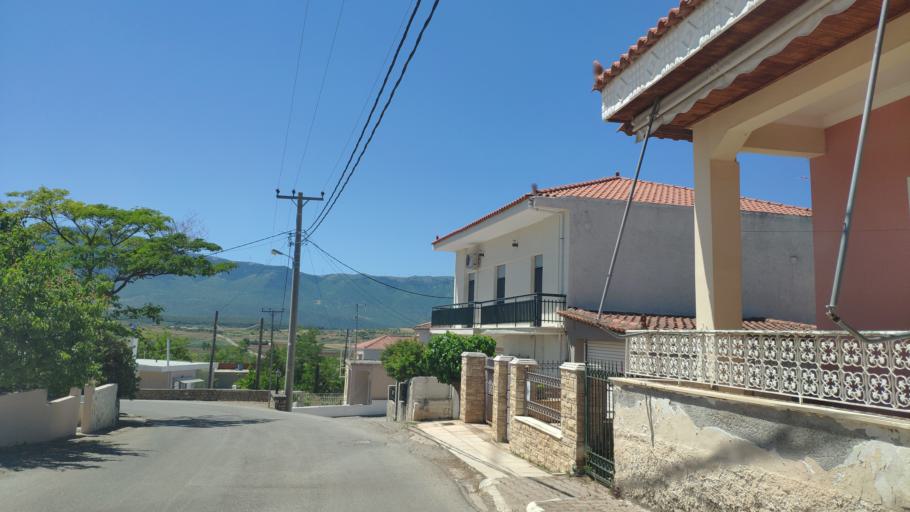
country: GR
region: Central Greece
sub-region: Nomos Voiotias
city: Kaparellion
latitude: 38.2656
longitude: 23.2361
